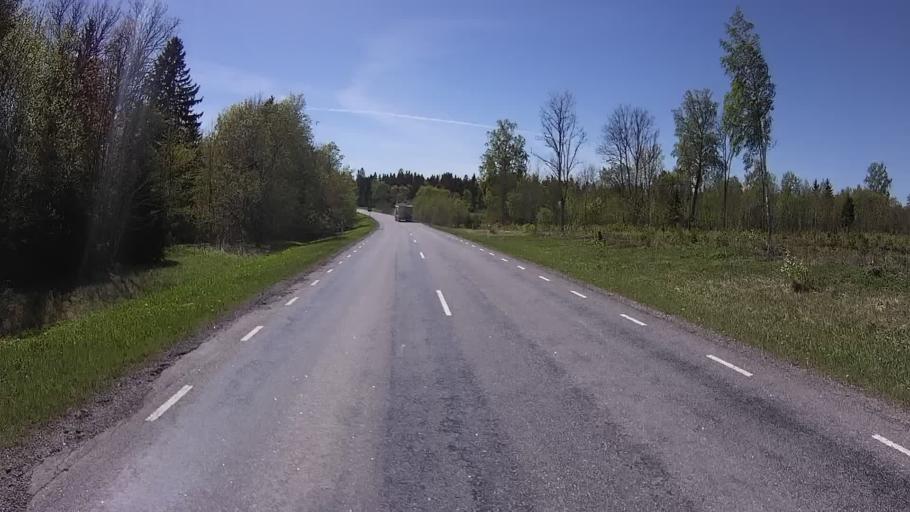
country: EE
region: Harju
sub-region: Raasiku vald
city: Raasiku
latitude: 59.0811
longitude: 25.1692
